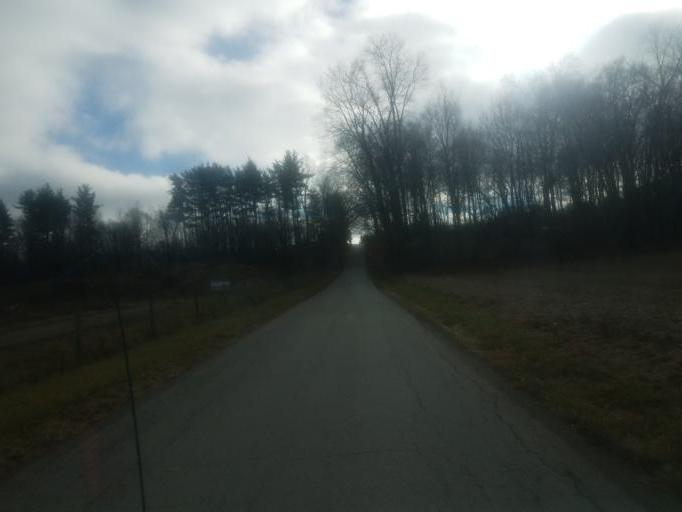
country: US
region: Ohio
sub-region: Sandusky County
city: Bellville
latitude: 40.6182
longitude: -82.5297
